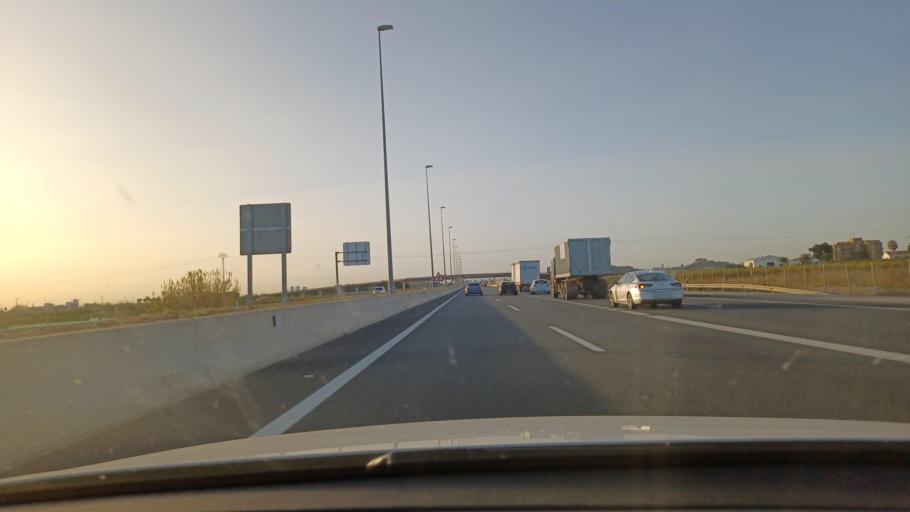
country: ES
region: Valencia
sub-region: Provincia de Valencia
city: Pucol
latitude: 39.6178
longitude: -0.2950
